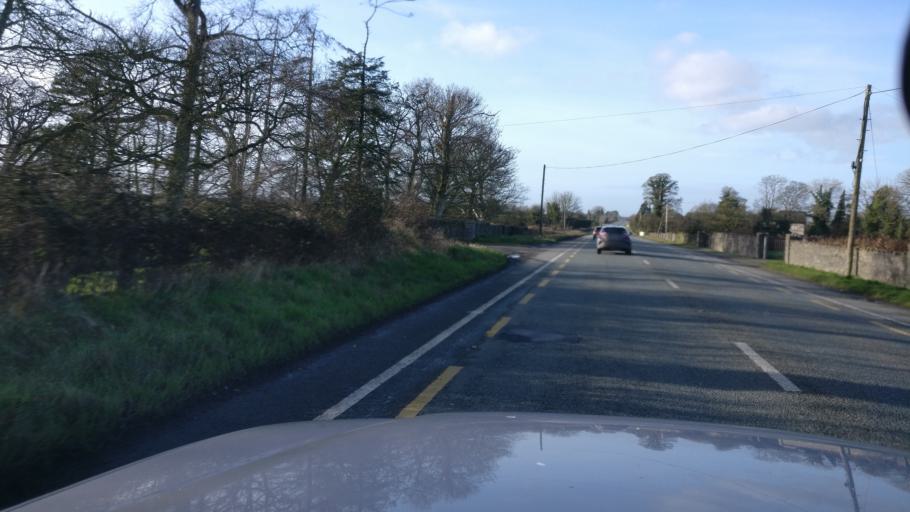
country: IE
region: Leinster
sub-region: Uibh Fhaili
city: Tullamore
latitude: 53.3086
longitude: -7.5455
